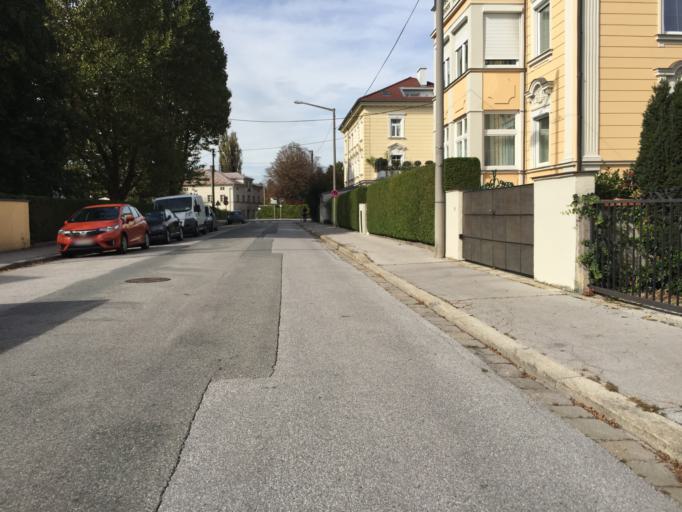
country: AT
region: Salzburg
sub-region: Salzburg Stadt
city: Salzburg
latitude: 47.8006
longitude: 13.0248
